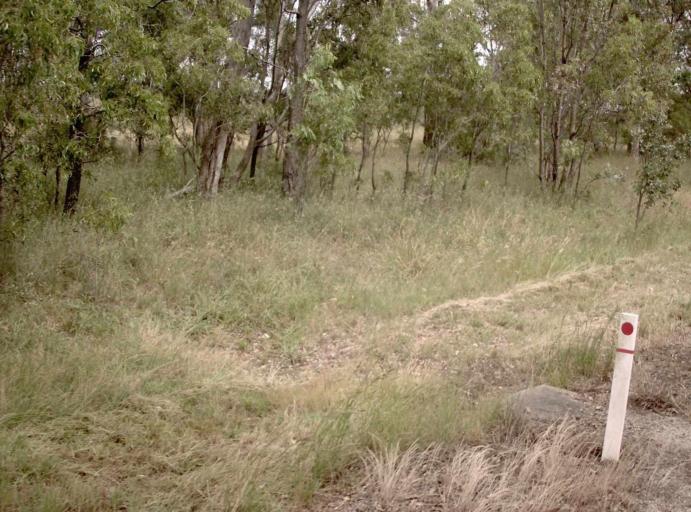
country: AU
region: Victoria
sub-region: Wellington
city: Sale
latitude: -37.9002
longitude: 147.0736
